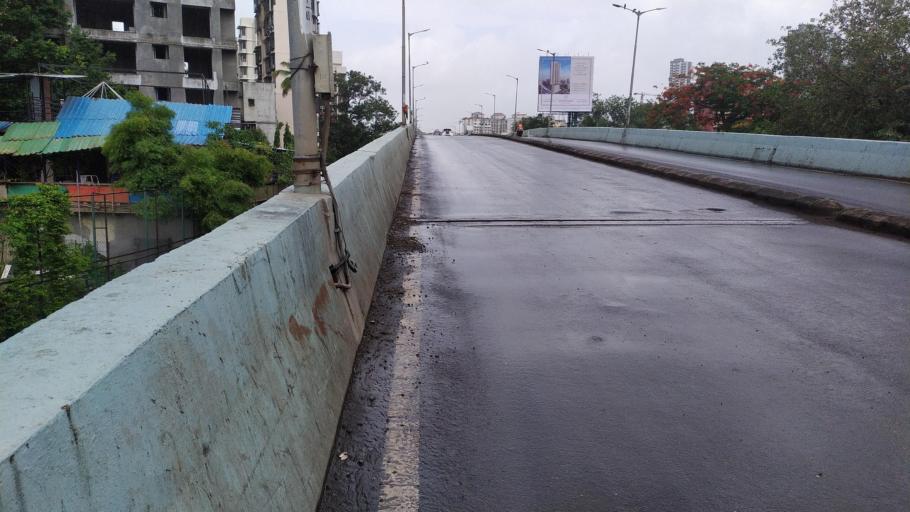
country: IN
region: Maharashtra
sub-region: Mumbai Suburban
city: Borivli
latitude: 19.2374
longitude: 72.8626
